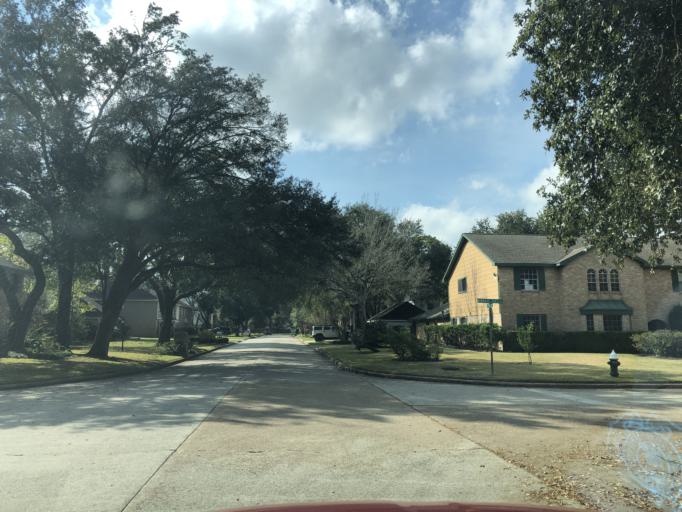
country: US
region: Texas
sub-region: Harris County
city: Tomball
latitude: 30.0264
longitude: -95.5441
